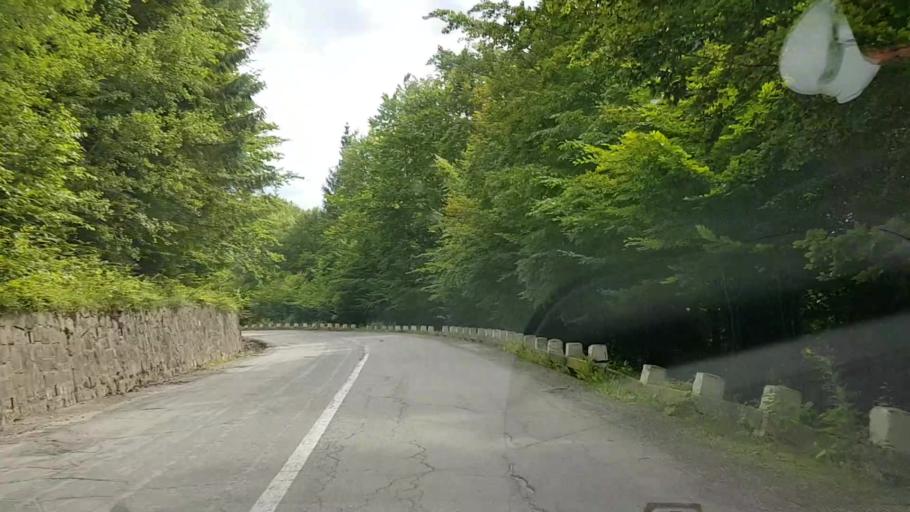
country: RO
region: Neamt
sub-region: Comuna Pangarati
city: Pangarati
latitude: 46.9849
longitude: 26.1147
